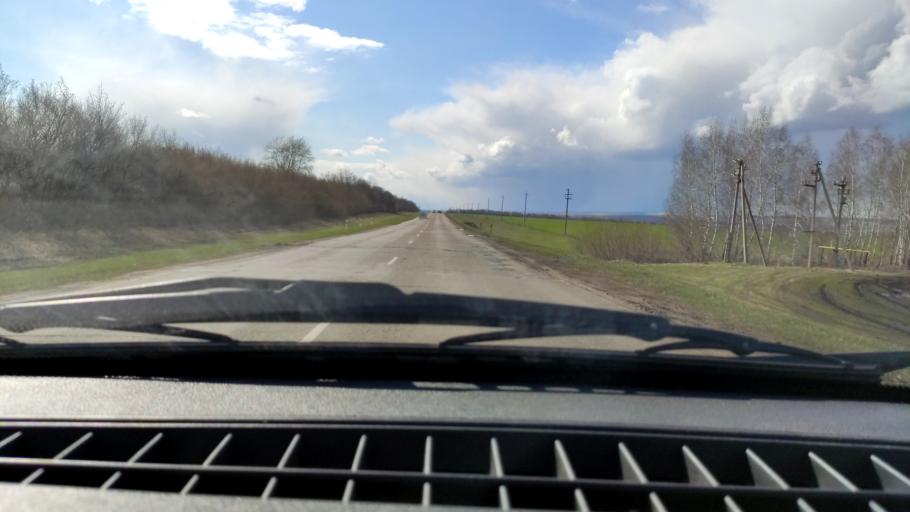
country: RU
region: Bashkortostan
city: Alekseyevka
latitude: 55.1057
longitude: 55.0023
